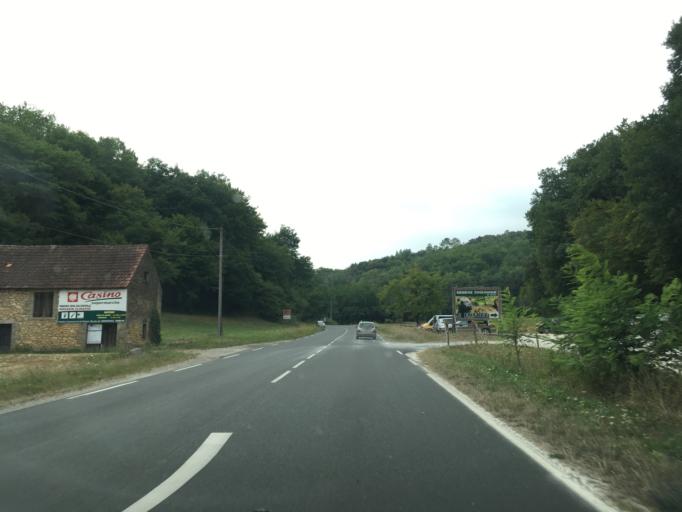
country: FR
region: Aquitaine
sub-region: Departement de la Dordogne
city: Carsac-Aillac
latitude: 44.8509
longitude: 1.3087
